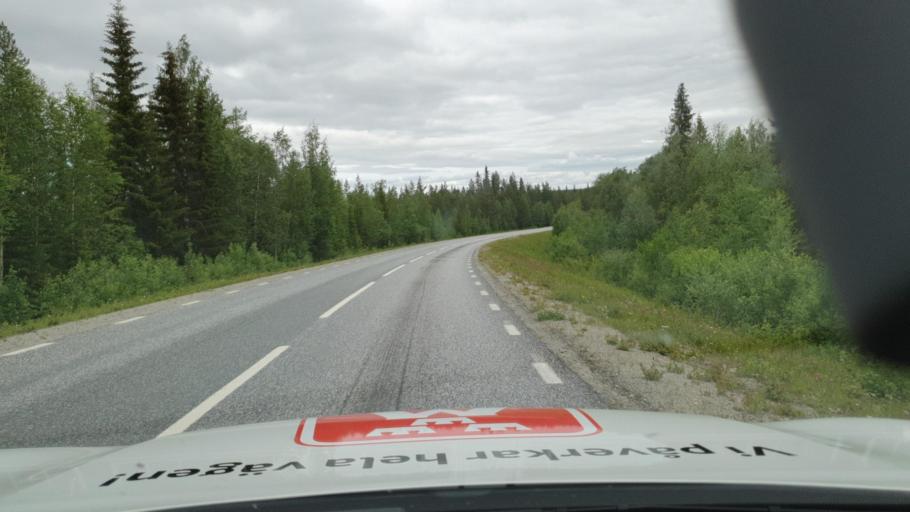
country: SE
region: Vaesterbotten
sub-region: Asele Kommun
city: Asele
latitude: 64.2072
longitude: 17.5108
